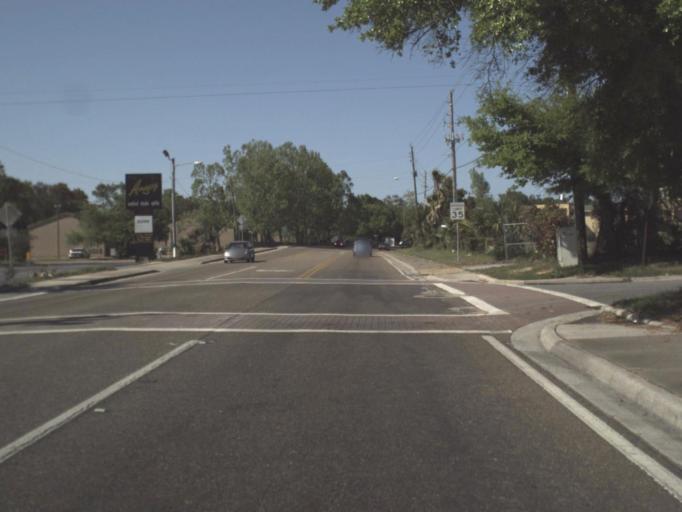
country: US
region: Florida
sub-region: Escambia County
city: East Pensacola Heights
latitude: 30.4315
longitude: -87.1755
